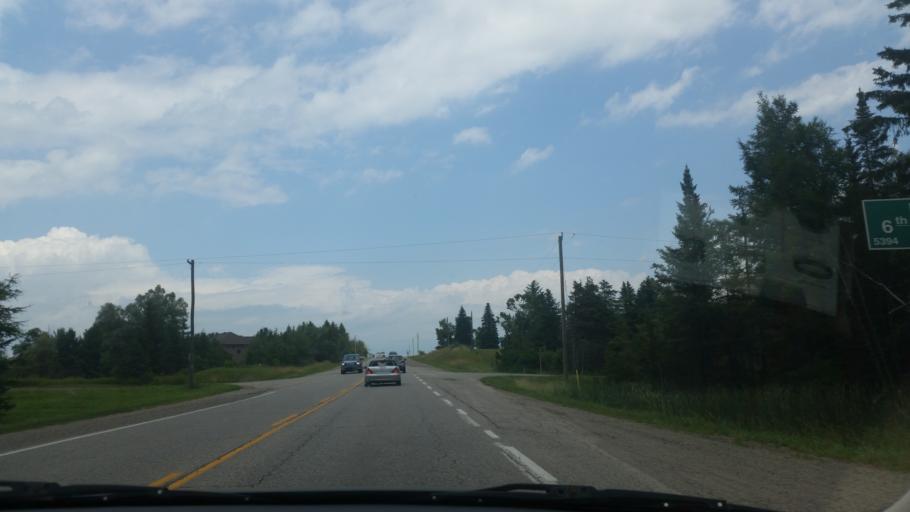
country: CA
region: Ontario
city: Orangeville
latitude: 43.7352
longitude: -80.0892
